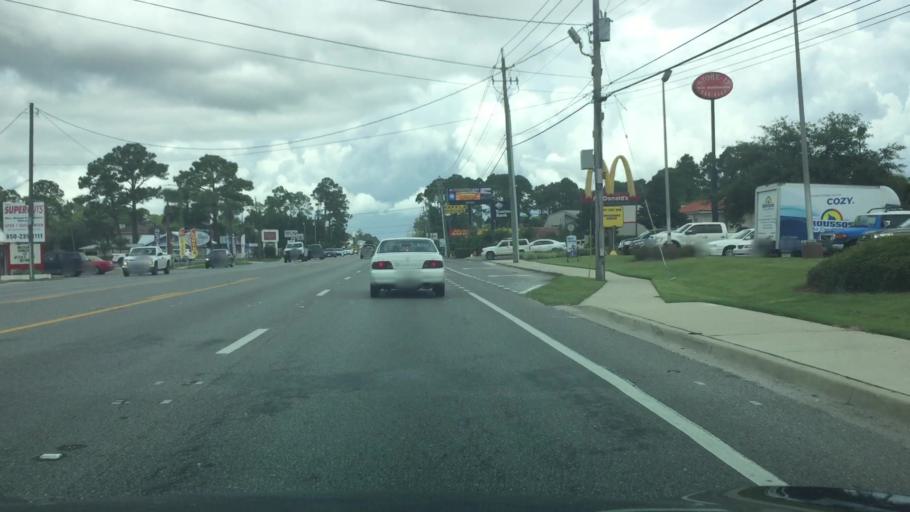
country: US
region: Florida
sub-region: Bay County
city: Upper Grand Lagoon
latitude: 30.1608
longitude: -85.7540
